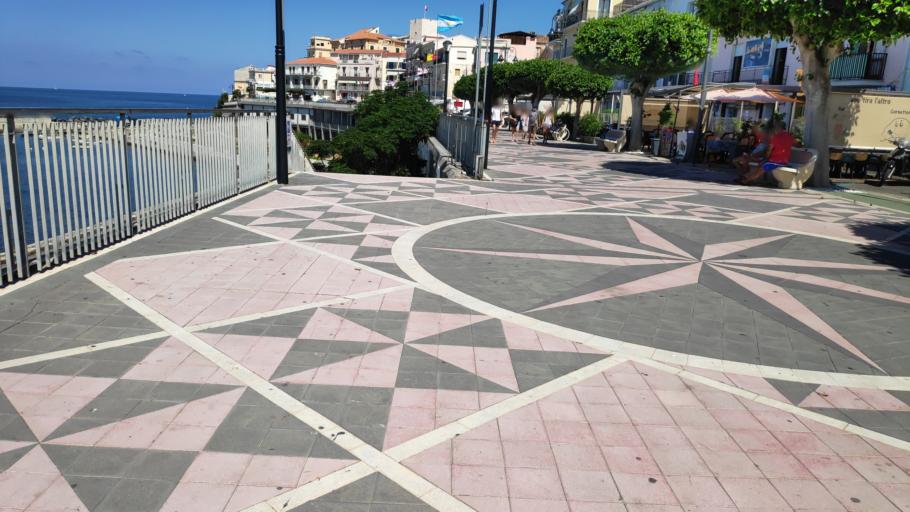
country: IT
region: Calabria
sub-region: Provincia di Cosenza
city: Diamante
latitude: 39.6769
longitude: 15.8187
